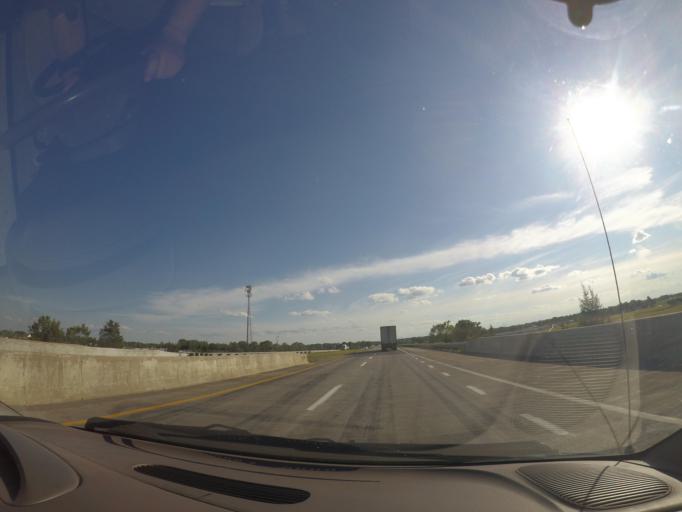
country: US
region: Ohio
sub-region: Henry County
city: Napoleon
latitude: 41.4063
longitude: -84.1353
